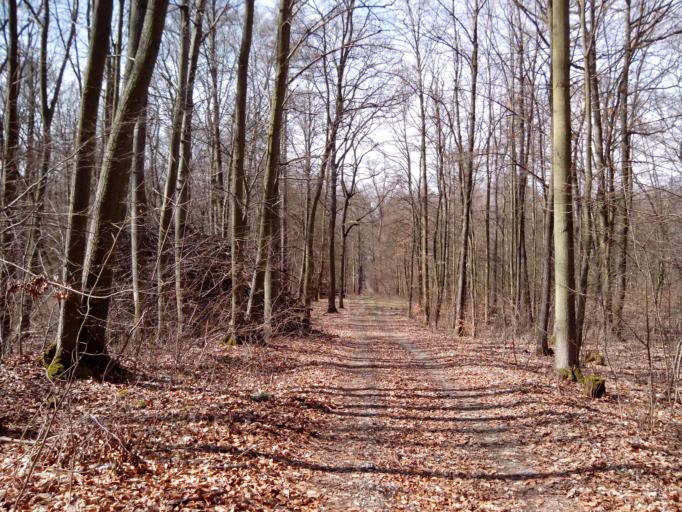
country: CZ
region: Central Bohemia
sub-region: Okres Beroun
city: Beroun
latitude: 49.9377
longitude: 14.1061
